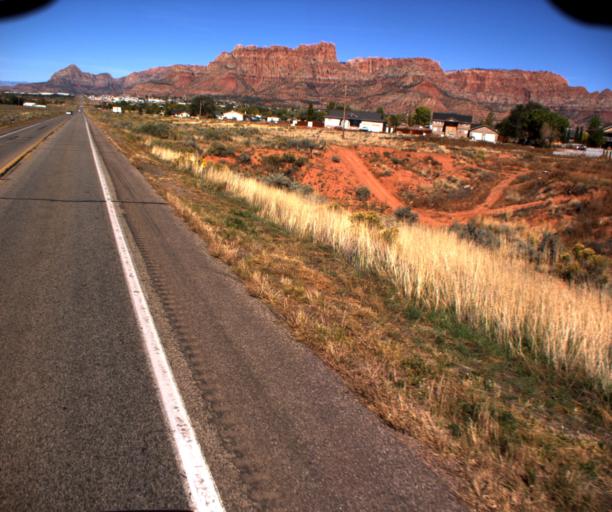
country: US
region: Arizona
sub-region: Mohave County
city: Colorado City
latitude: 36.9739
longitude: -112.9777
